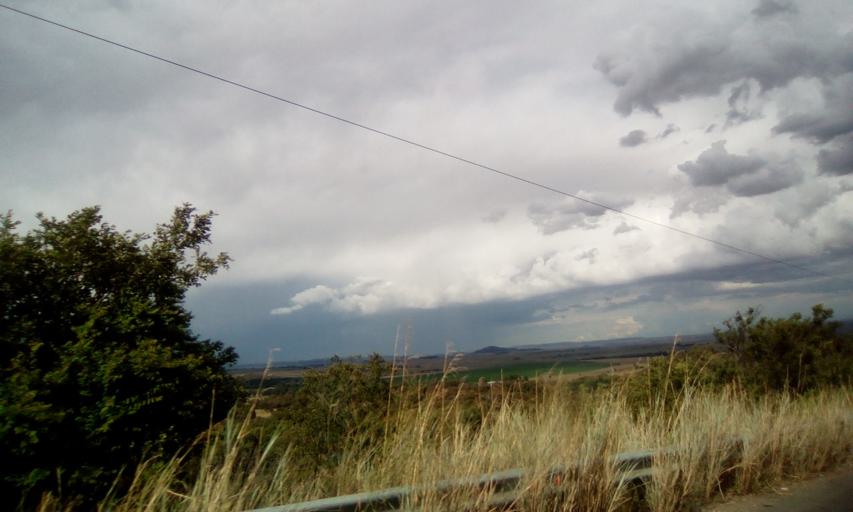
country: ZA
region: Orange Free State
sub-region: Thabo Mofutsanyana District Municipality
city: Ladybrand
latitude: -29.2124
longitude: 27.4584
